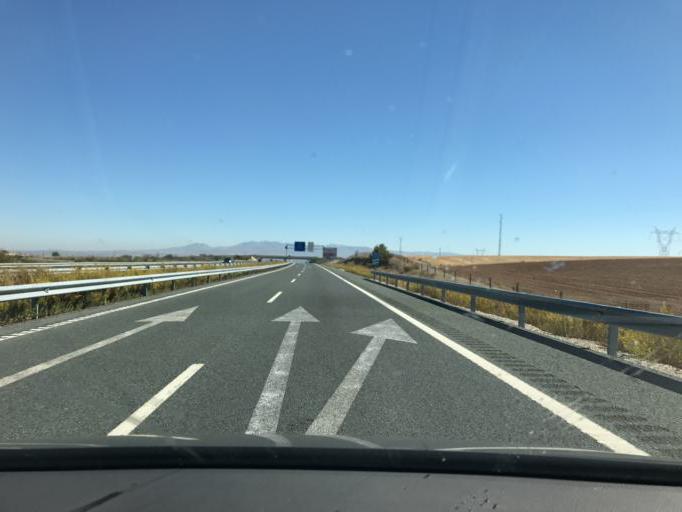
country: ES
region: Andalusia
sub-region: Provincia de Granada
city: Darro
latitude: 37.3212
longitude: -3.2755
